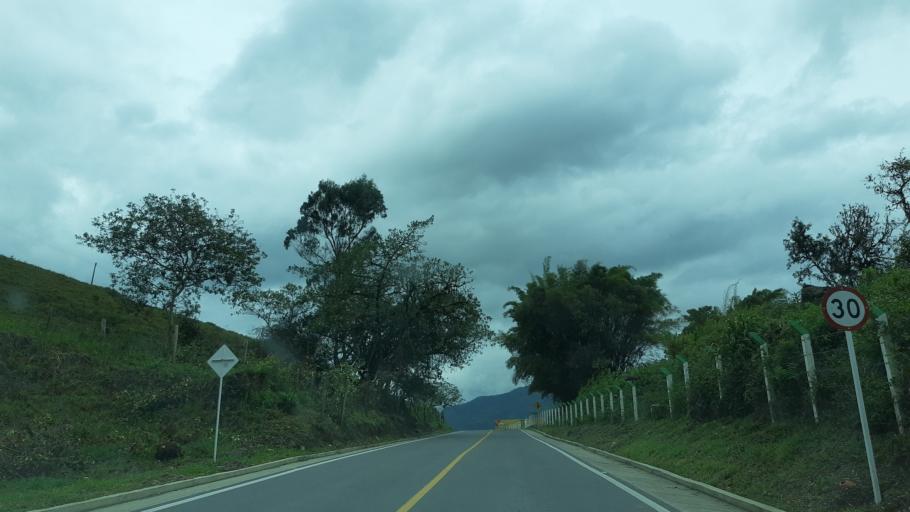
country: CO
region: Boyaca
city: Chivor
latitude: 4.9746
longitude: -73.3307
